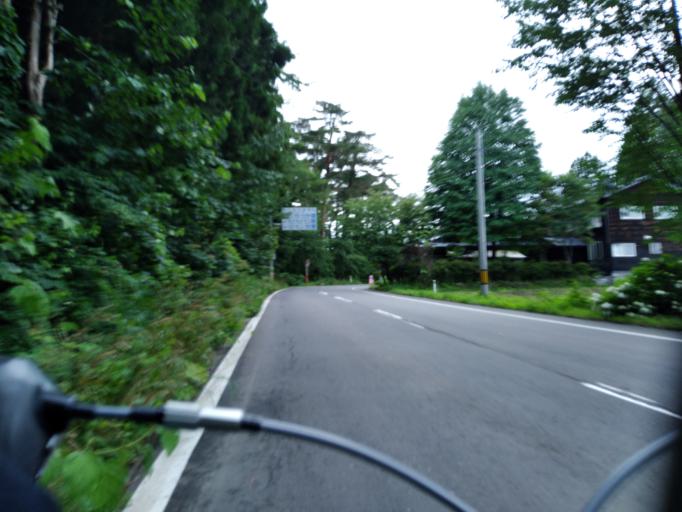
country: JP
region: Iwate
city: Morioka-shi
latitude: 39.8125
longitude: 141.0699
